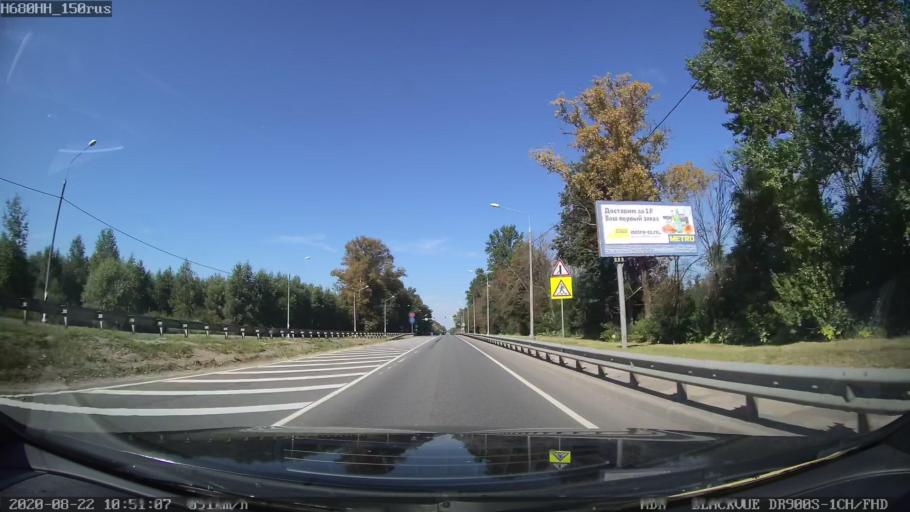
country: RU
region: Tverskaya
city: Emmaus
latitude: 56.7868
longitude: 36.0854
